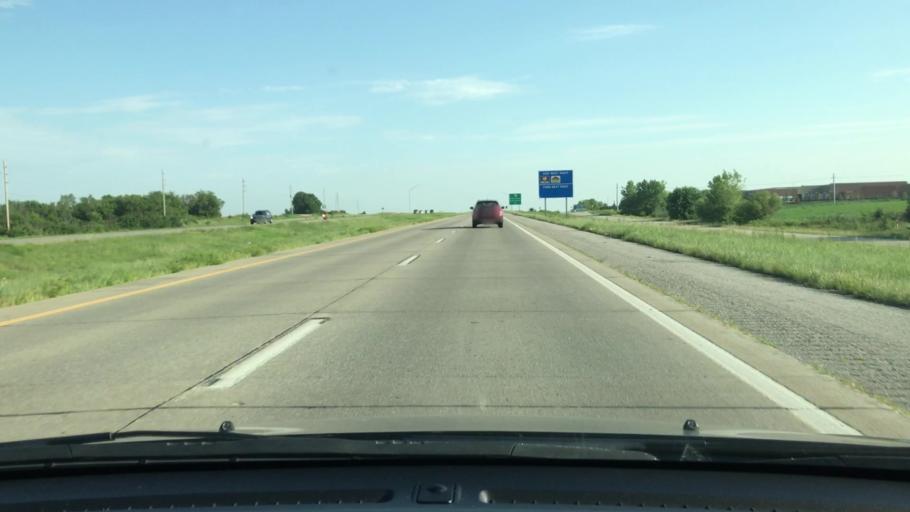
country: US
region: Missouri
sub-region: Jackson County
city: Greenwood
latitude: 38.8611
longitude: -94.3755
